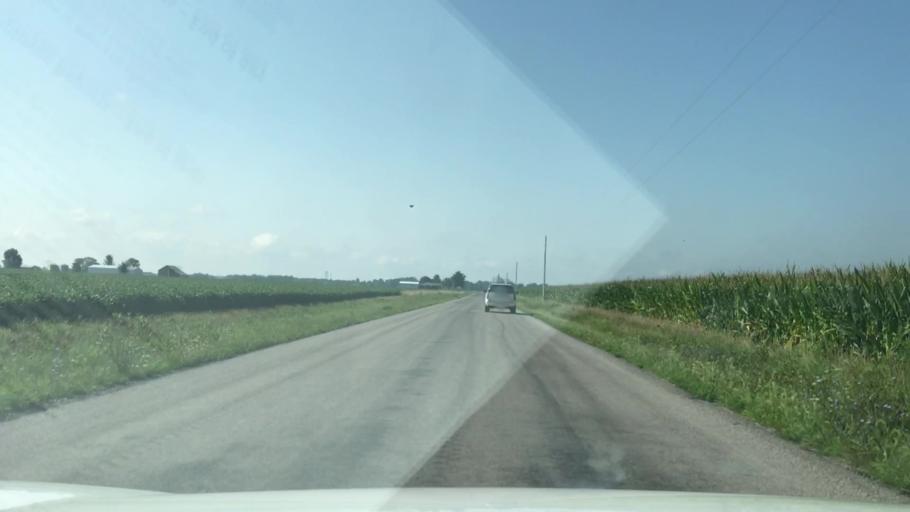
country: US
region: Illinois
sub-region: Washington County
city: Okawville
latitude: 38.4111
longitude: -89.4866
